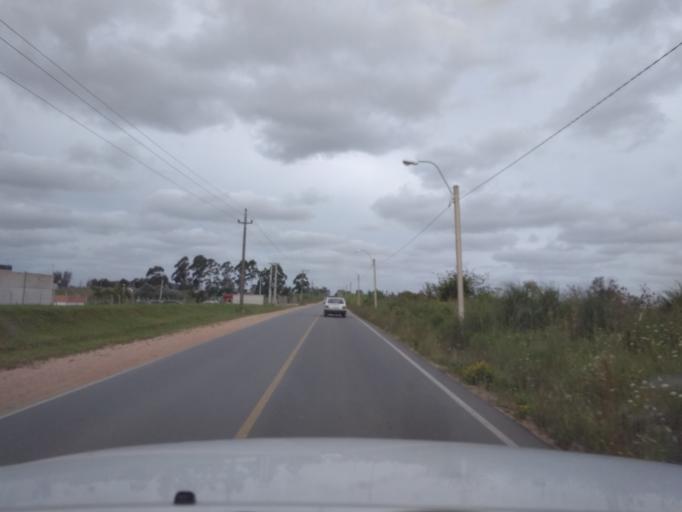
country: UY
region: Canelones
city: Colonia Nicolich
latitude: -34.7858
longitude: -56.0054
